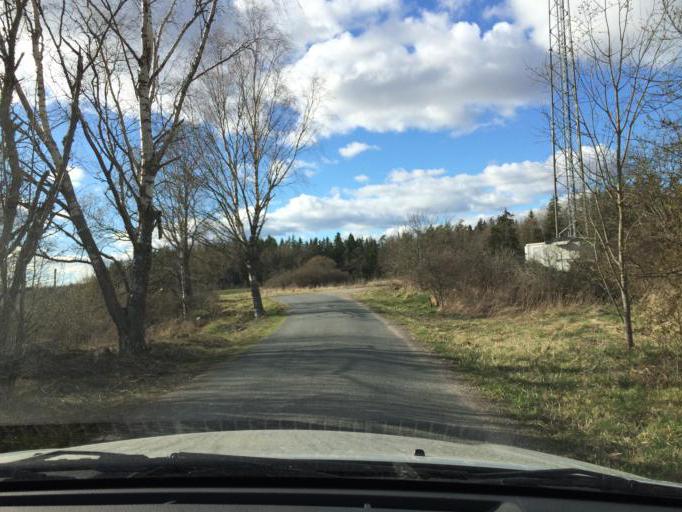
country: SE
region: Soedermanland
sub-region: Eskilstuna Kommun
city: Hallbybrunn
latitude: 59.4291
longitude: 16.4035
